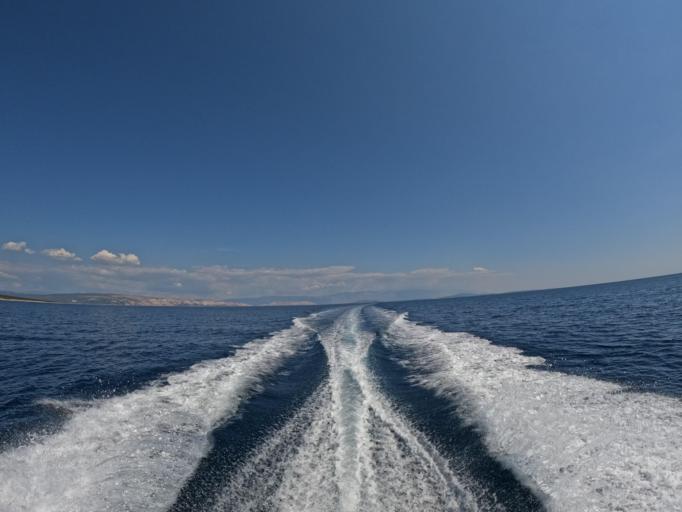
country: HR
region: Primorsko-Goranska
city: Cres
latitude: 44.9365
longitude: 14.5066
